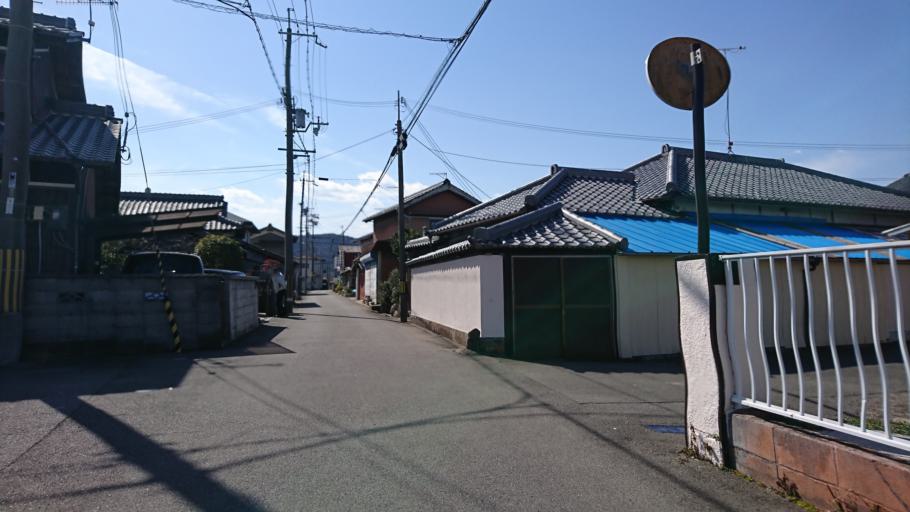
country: JP
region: Hyogo
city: Kakogawacho-honmachi
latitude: 34.8106
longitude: 134.8138
